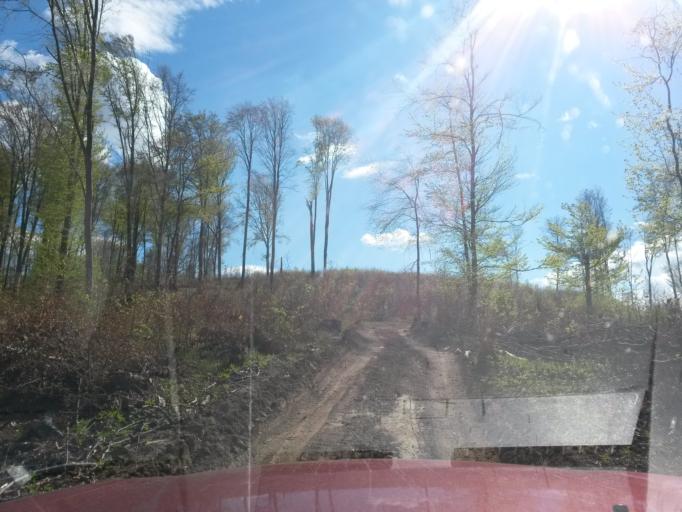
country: SK
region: Presovsky
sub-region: Okres Presov
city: Presov
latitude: 48.9433
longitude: 21.1320
